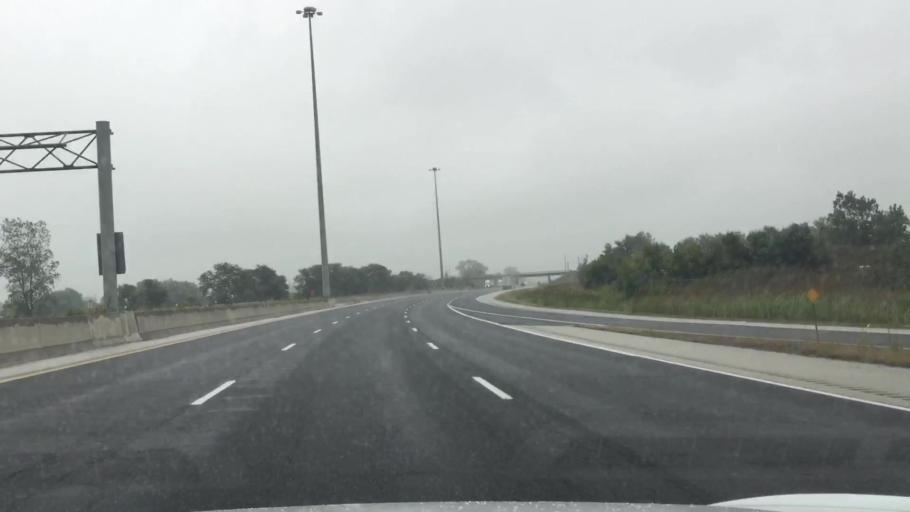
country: CA
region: Ontario
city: Windsor
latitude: 42.2476
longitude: -82.9528
